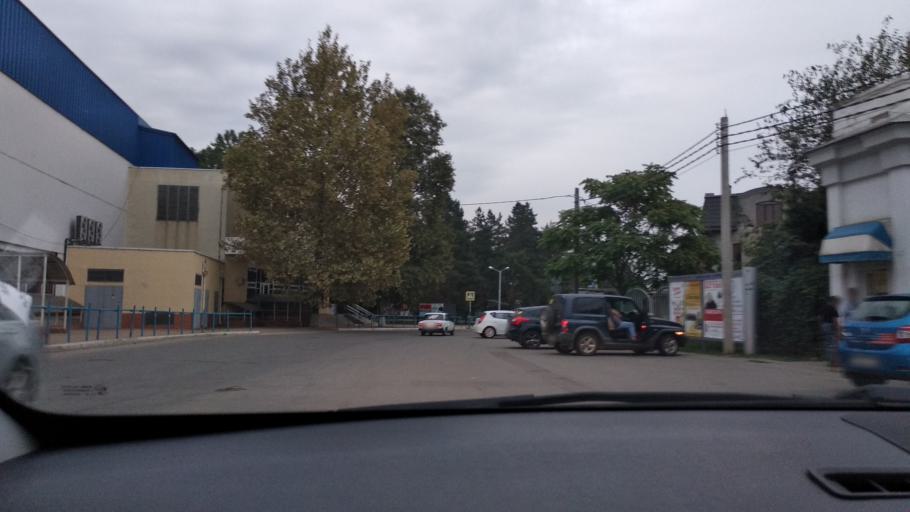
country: RU
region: Adygeya
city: Yablonovskiy
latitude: 45.0161
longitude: 38.9552
